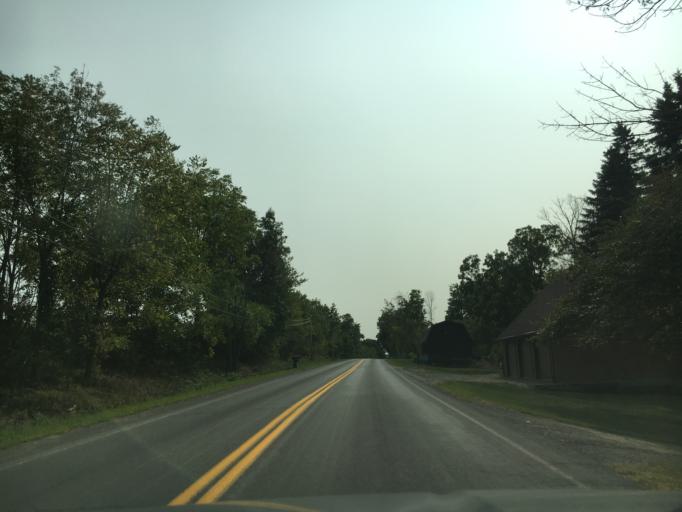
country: US
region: New York
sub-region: Steuben County
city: Sylvan Beach
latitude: 42.4624
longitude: -77.0979
